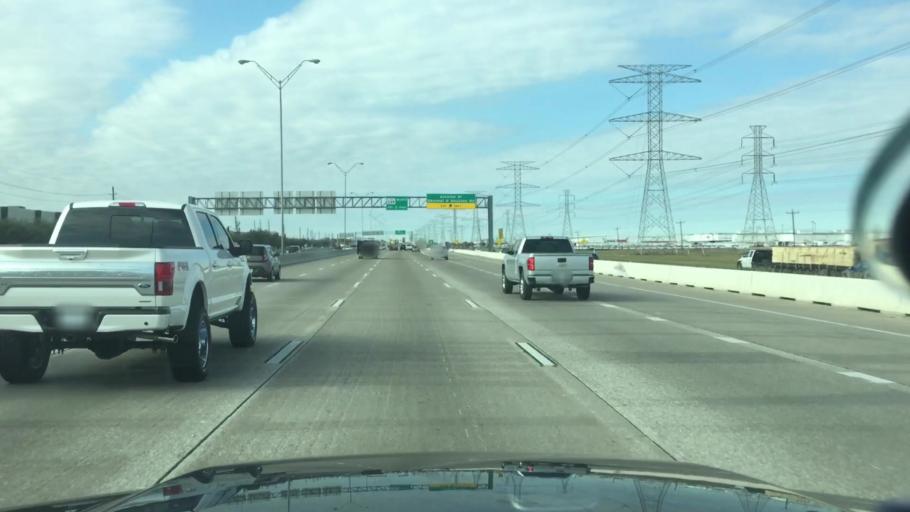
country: US
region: Texas
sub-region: Harris County
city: Hudson
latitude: 29.9377
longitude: -95.4743
